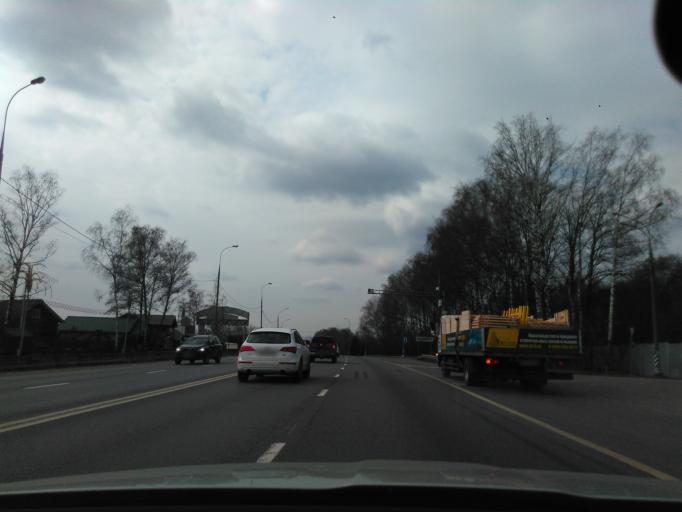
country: RU
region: Moskovskaya
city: Sheremet'yevskiy
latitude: 56.0052
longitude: 37.5406
